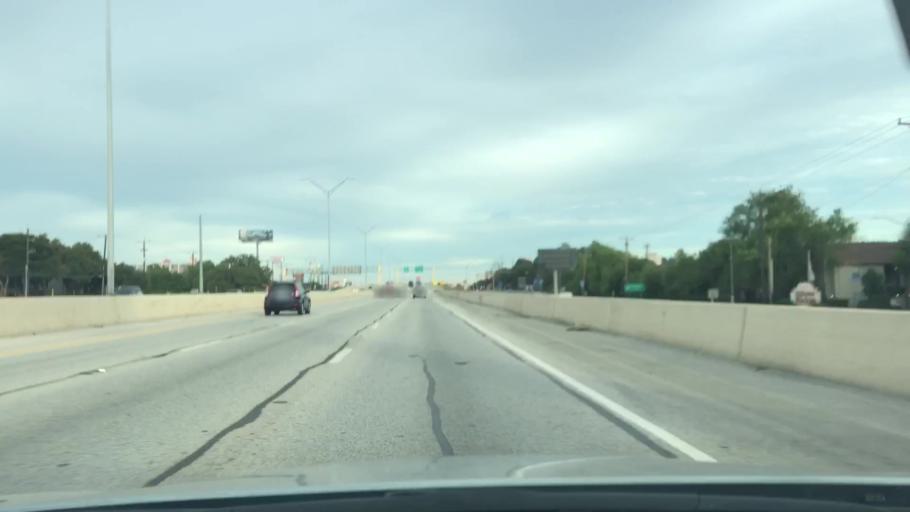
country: US
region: Texas
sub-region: Bexar County
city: Windcrest
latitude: 29.5160
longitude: -98.4171
